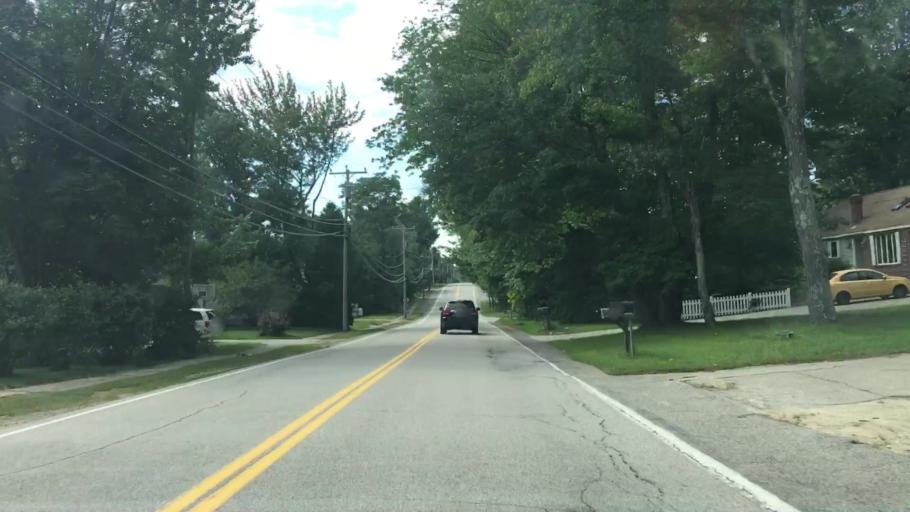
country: US
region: New Hampshire
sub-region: Strafford County
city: Somersworth
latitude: 43.2587
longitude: -70.8734
